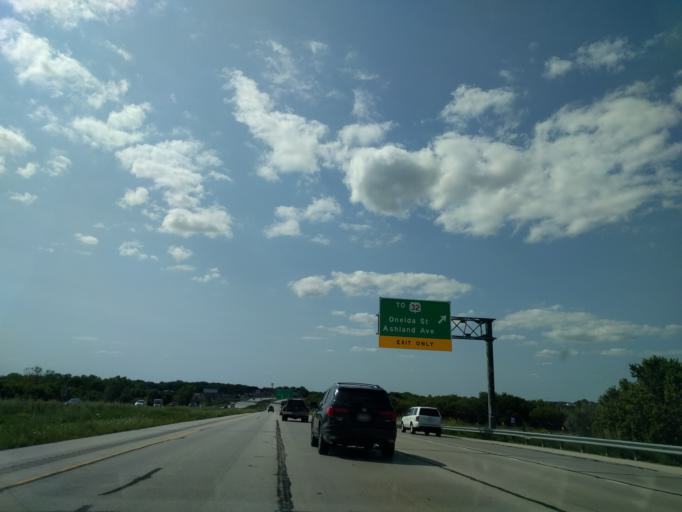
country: US
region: Wisconsin
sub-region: Brown County
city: Ashwaubenon
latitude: 44.4783
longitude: -88.0601
